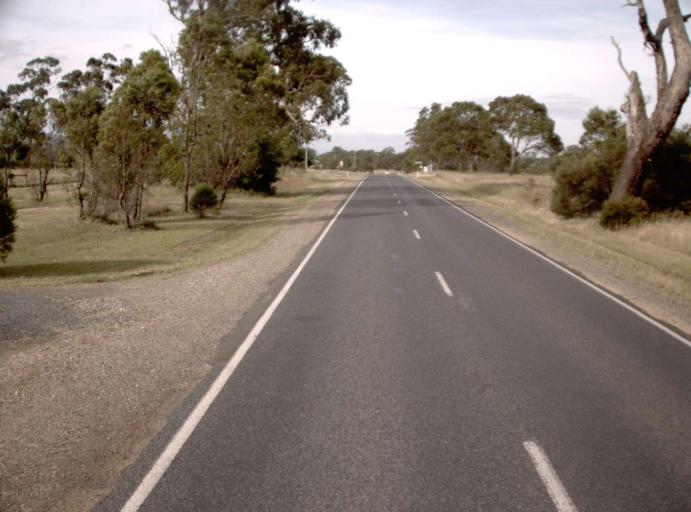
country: AU
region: Victoria
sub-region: Latrobe
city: Traralgon
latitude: -38.0671
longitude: 146.6173
